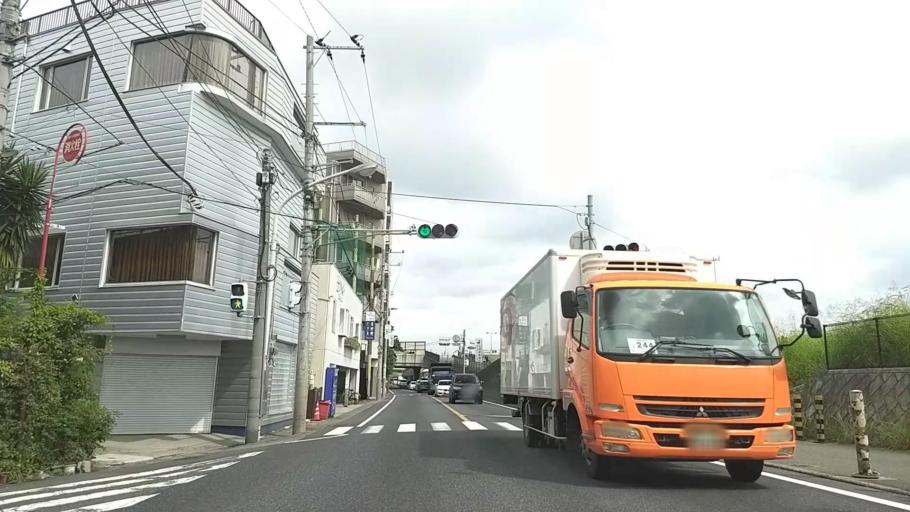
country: JP
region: Kanagawa
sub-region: Kawasaki-shi
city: Kawasaki
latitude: 35.5828
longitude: 139.6668
